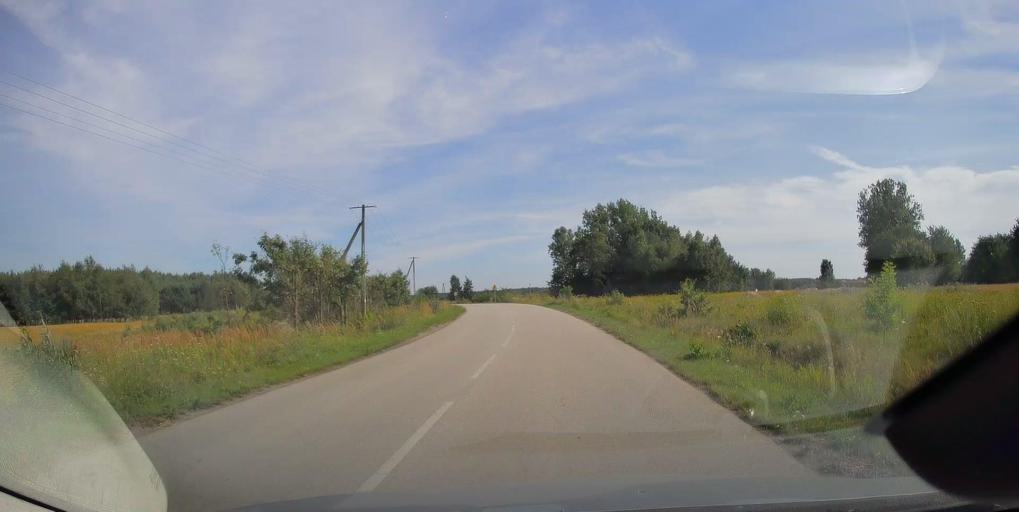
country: PL
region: Lodz Voivodeship
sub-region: Powiat opoczynski
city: Mniszkow
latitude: 51.3532
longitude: 20.0388
